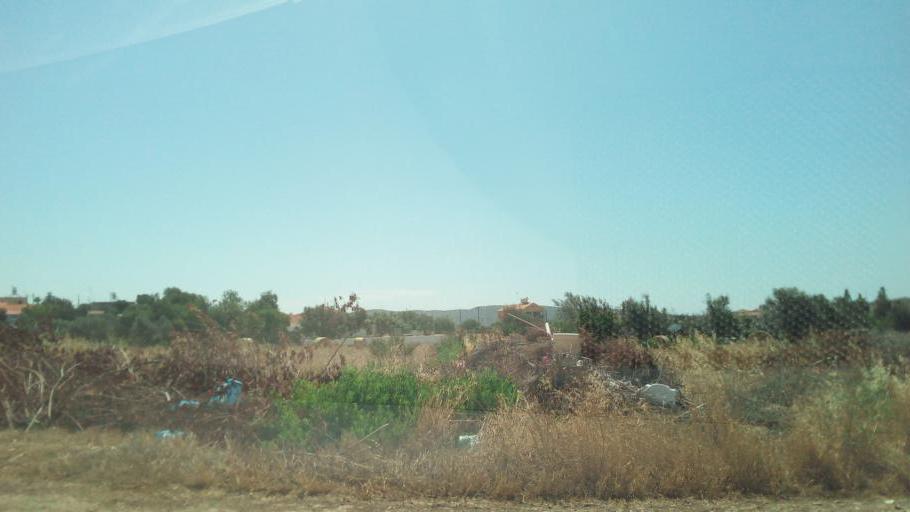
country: CY
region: Limassol
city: Pyrgos
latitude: 34.7366
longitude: 33.1813
